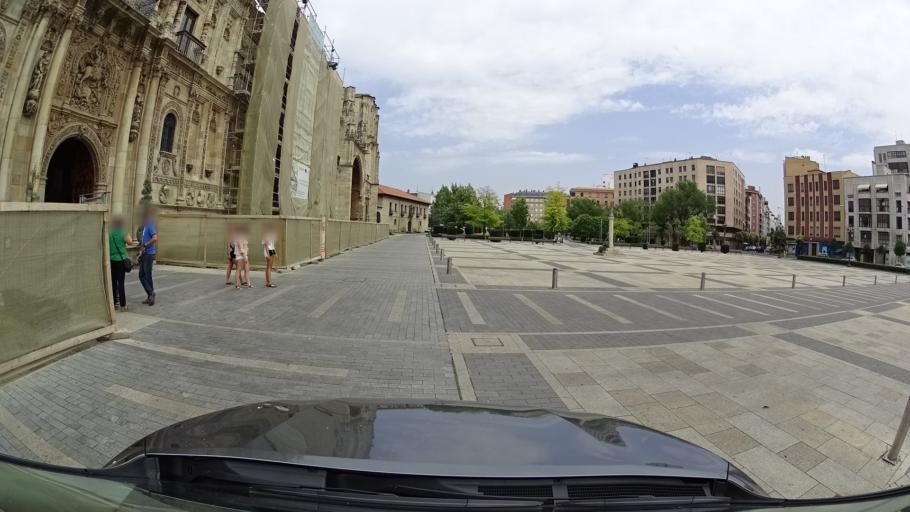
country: ES
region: Castille and Leon
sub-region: Provincia de Leon
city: Leon
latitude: 42.6016
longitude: -5.5820
